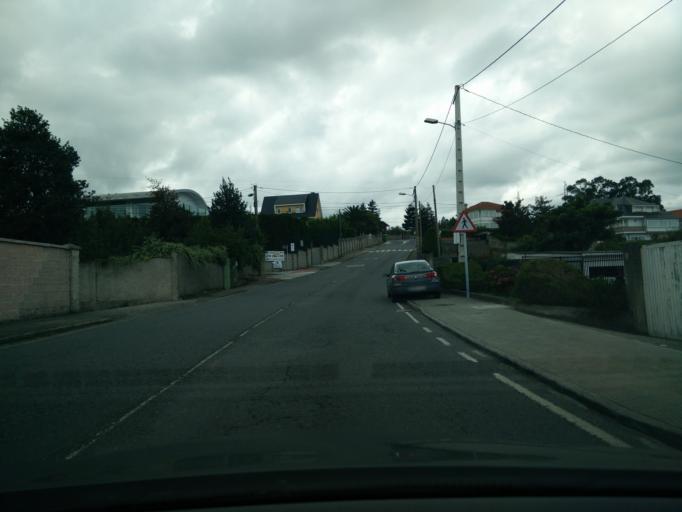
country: ES
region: Galicia
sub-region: Provincia da Coruna
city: Culleredo
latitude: 43.3258
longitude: -8.4038
